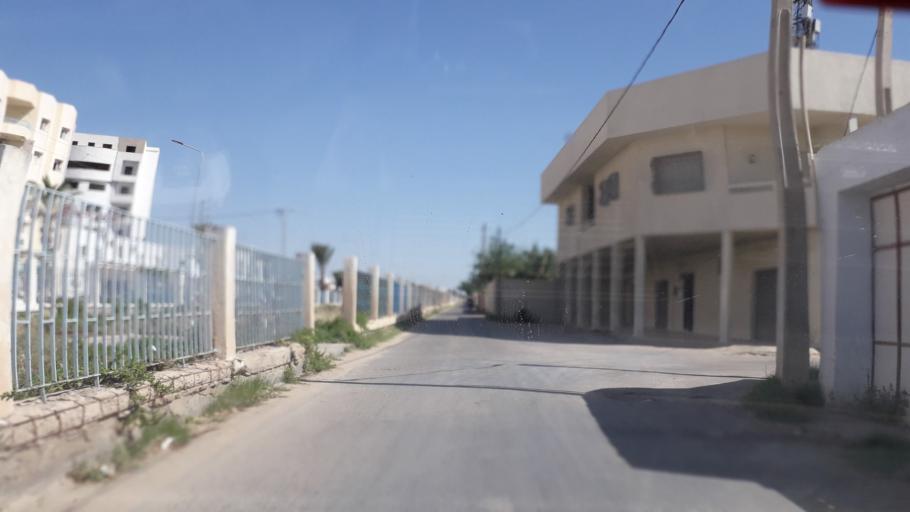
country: TN
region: Safaqis
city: Al Qarmadah
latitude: 34.8082
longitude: 10.7619
